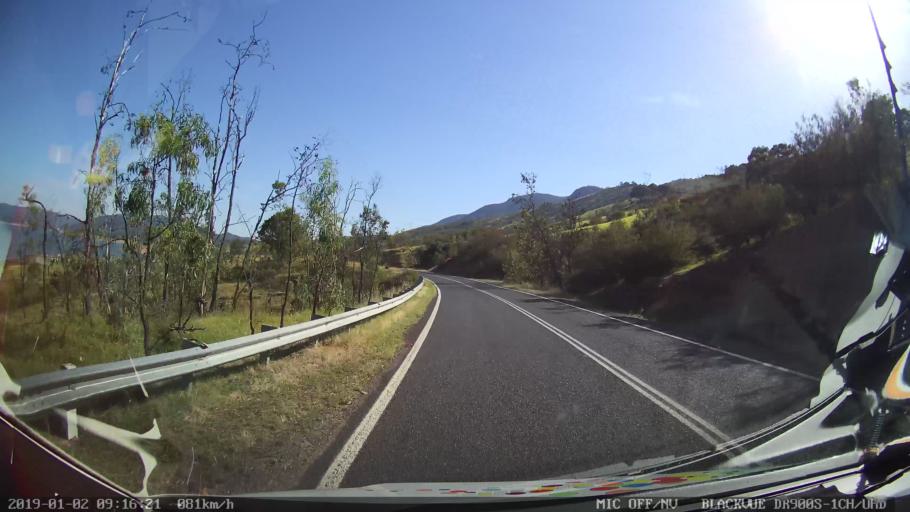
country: AU
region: New South Wales
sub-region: Tumut Shire
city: Tumut
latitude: -35.4544
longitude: 148.2836
